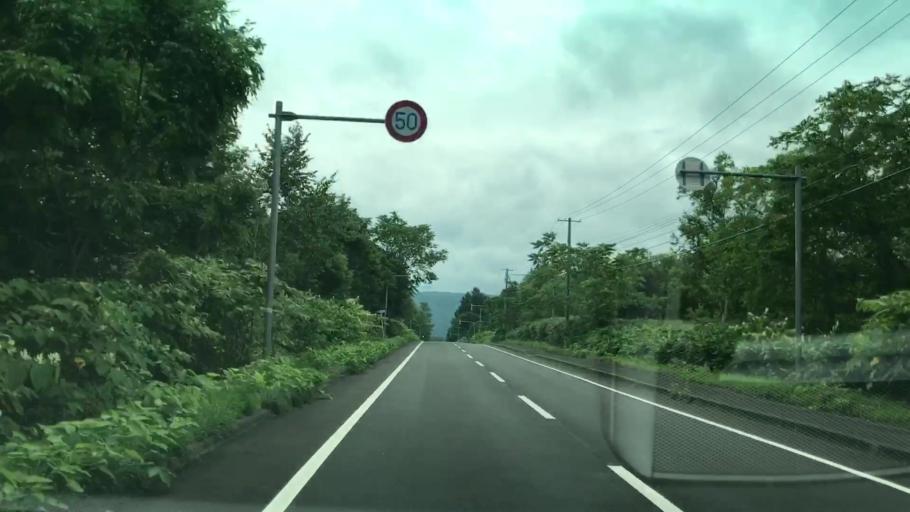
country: JP
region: Hokkaido
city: Yoichi
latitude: 43.0689
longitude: 140.8187
